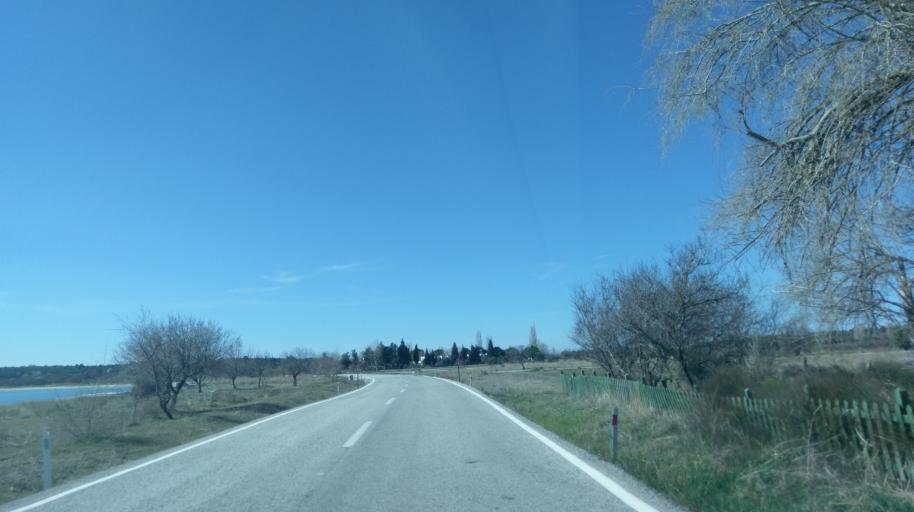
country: TR
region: Canakkale
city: Intepe
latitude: 40.0538
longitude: 26.2094
